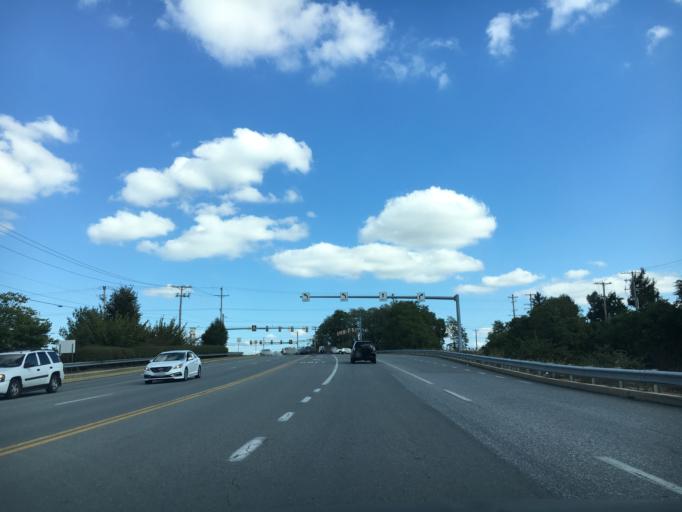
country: US
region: Pennsylvania
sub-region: York County
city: East York
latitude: 39.9830
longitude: -76.6669
